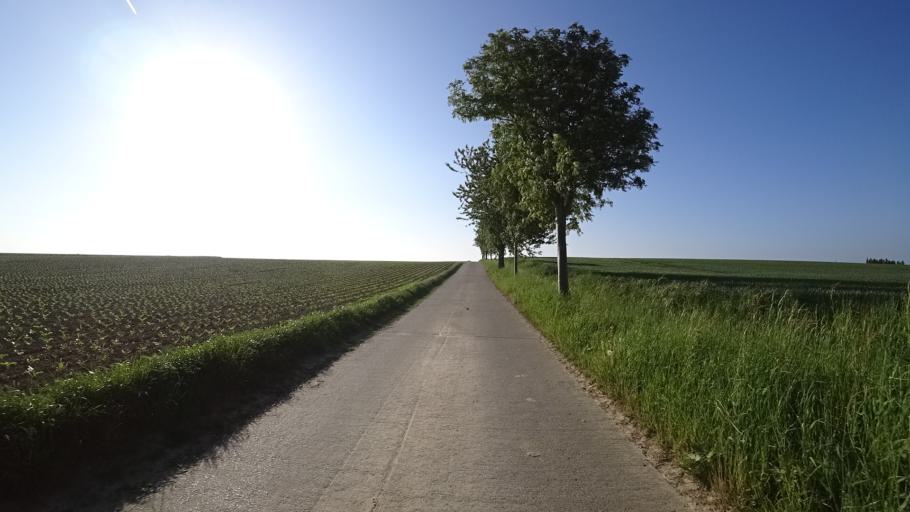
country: BE
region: Wallonia
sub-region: Province du Brabant Wallon
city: Walhain-Saint-Paul
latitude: 50.6232
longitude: 4.7048
